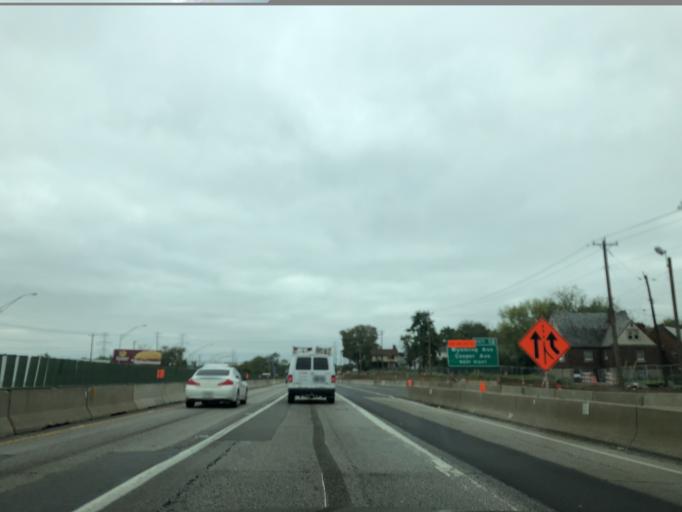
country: US
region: Ohio
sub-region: Hamilton County
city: Lockland
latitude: 39.2326
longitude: -84.4503
